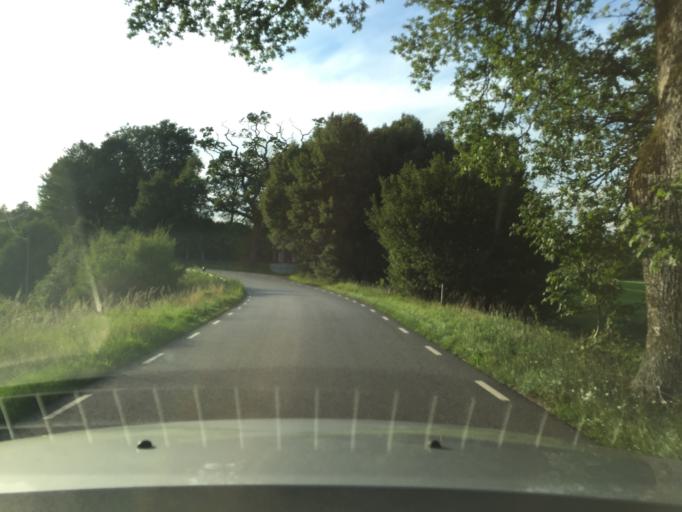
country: SE
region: Skane
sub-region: Hassleholms Kommun
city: Sosdala
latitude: 56.0536
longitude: 13.6272
